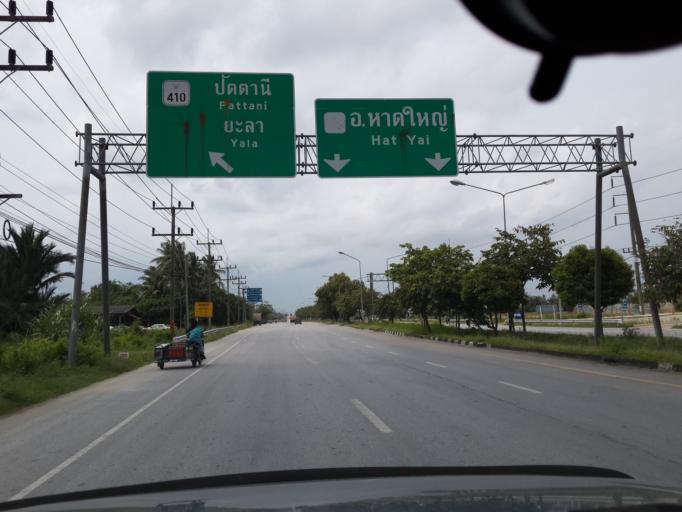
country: TH
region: Pattani
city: Pattani
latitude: 6.8515
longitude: 101.2594
